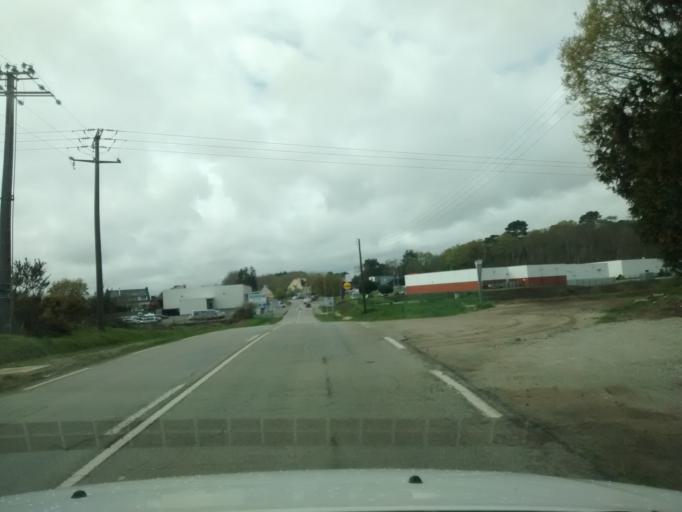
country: FR
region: Brittany
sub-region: Departement du Morbihan
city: Gestel
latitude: 47.7981
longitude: -3.4740
